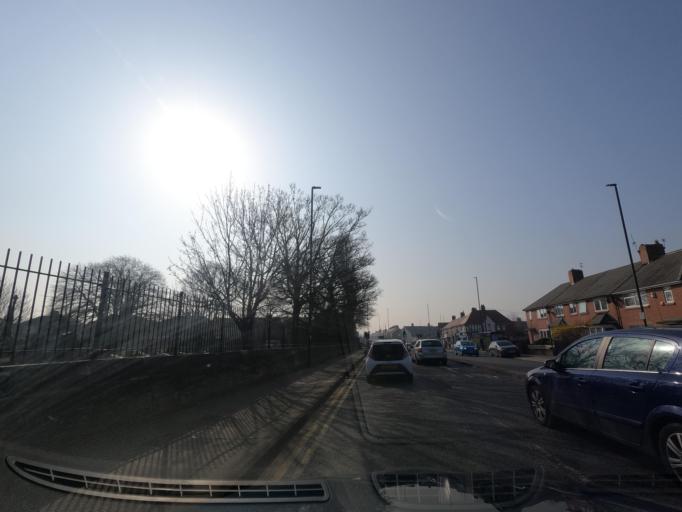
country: GB
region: England
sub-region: Newcastle upon Tyne
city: Gosforth
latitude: 54.9939
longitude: -1.5796
